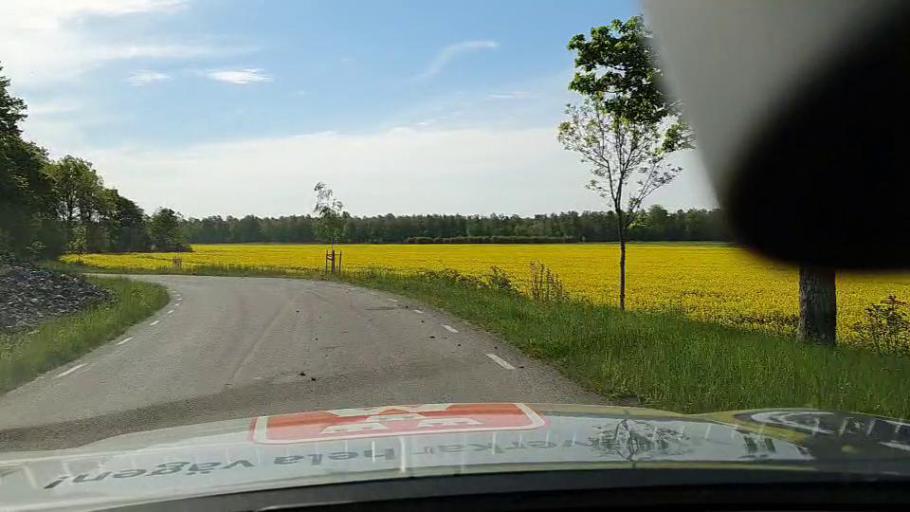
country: SE
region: Soedermanland
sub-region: Eskilstuna Kommun
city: Arla
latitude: 59.2574
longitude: 16.6800
